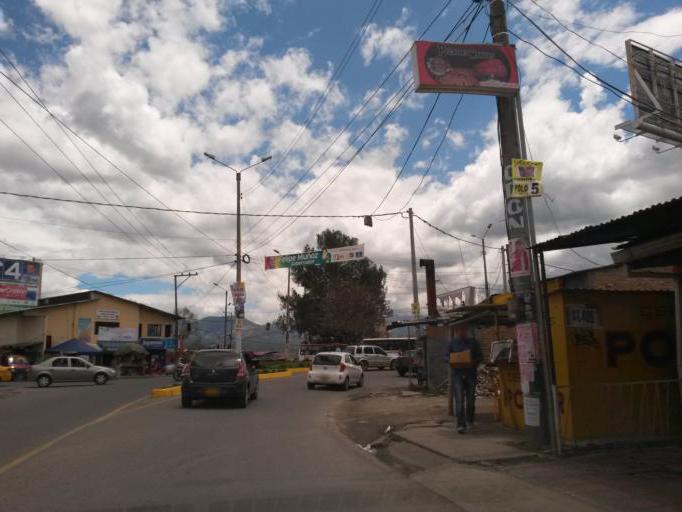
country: CO
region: Cauca
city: Popayan
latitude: 2.4816
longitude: -76.5749
